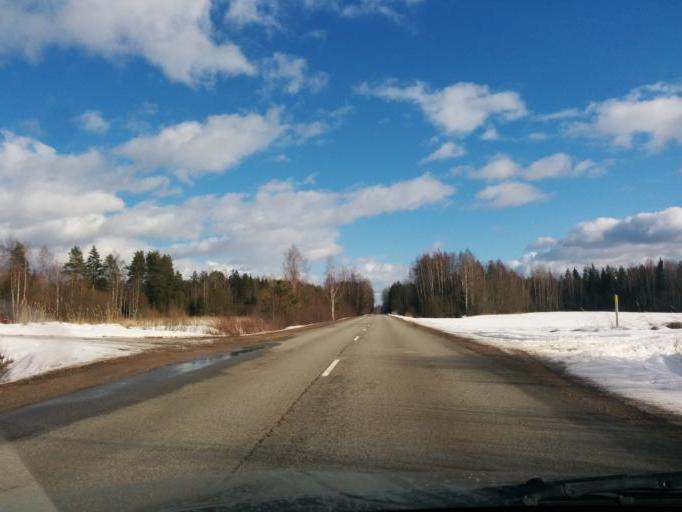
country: LV
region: Gulbenes Rajons
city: Gulbene
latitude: 57.1929
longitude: 26.9611
